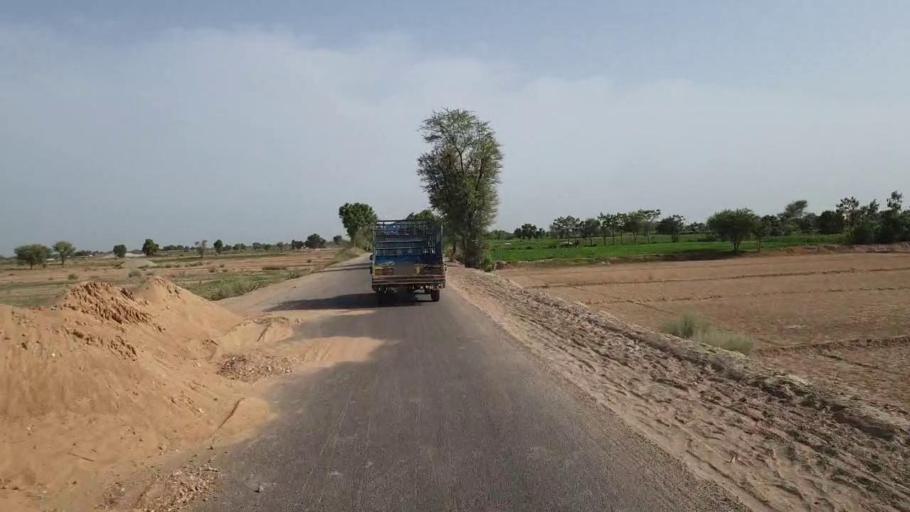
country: PK
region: Sindh
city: Sakrand
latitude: 26.2594
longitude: 68.2848
